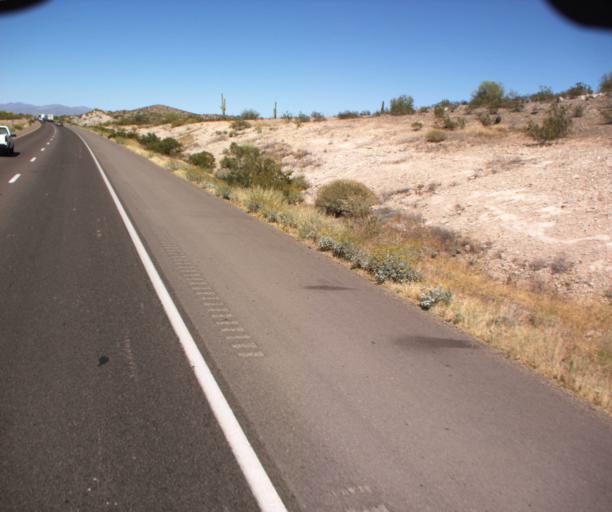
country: US
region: Arizona
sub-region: Maricopa County
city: Buckeye
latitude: 33.2458
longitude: -112.6379
